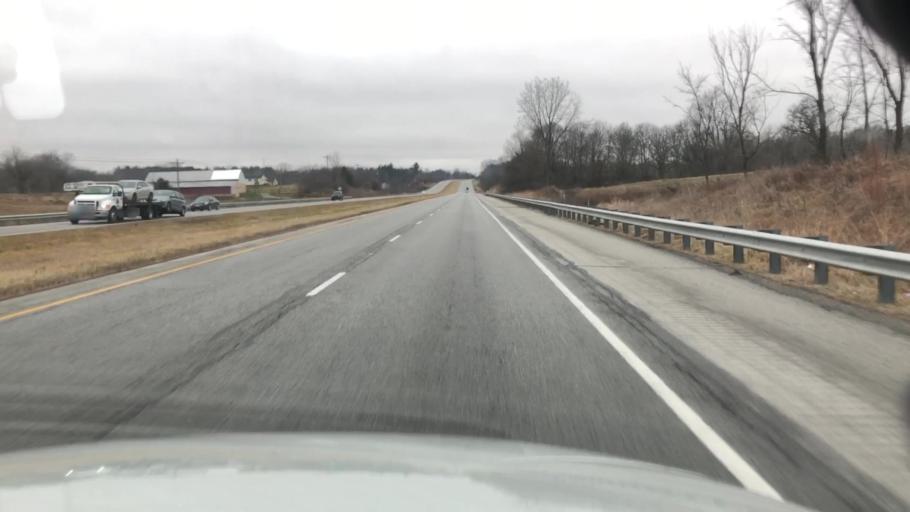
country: US
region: Indiana
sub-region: Whitley County
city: South Whitley
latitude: 41.1780
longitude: -85.5996
